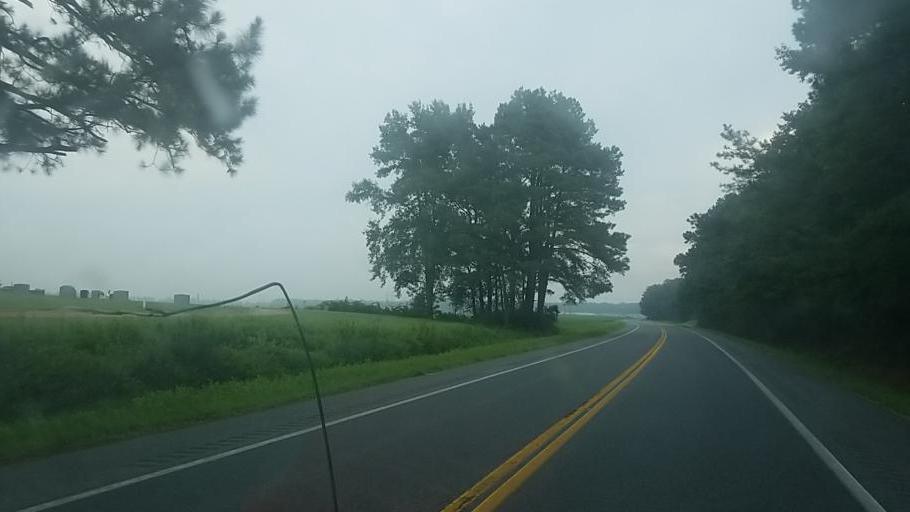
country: US
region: Maryland
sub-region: Wicomico County
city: Pittsville
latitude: 38.4519
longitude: -75.4170
